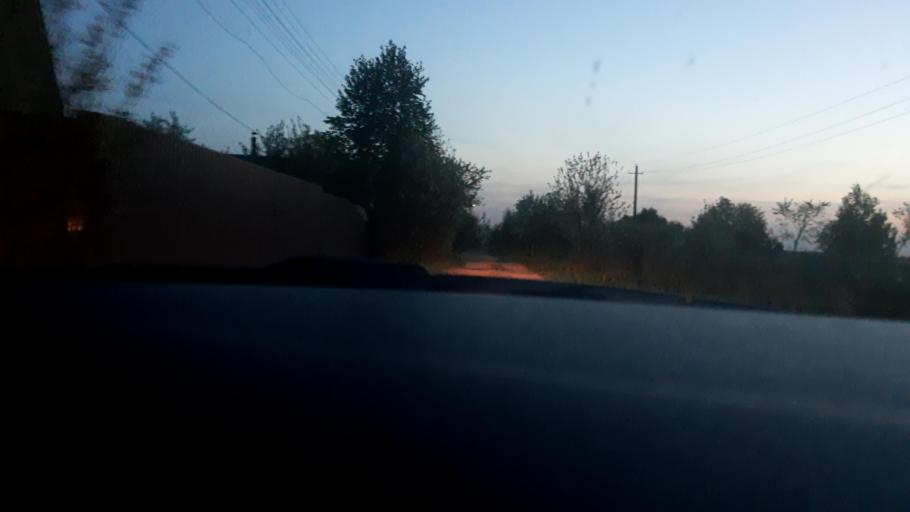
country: RU
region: Bashkortostan
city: Iglino
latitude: 54.7585
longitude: 56.3332
